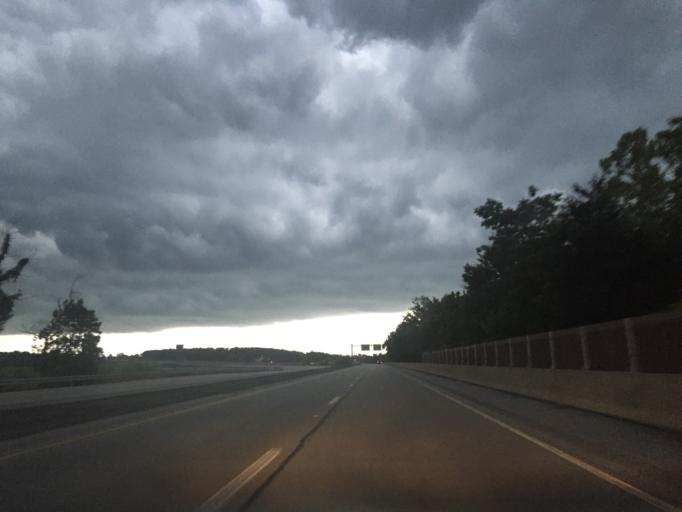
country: US
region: Pennsylvania
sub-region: York County
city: Spry
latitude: 39.9226
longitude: -76.7067
